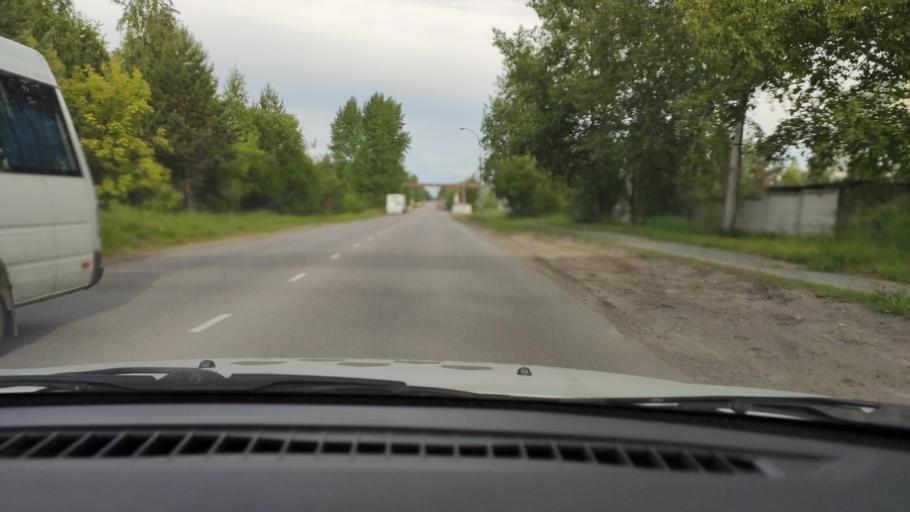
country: RU
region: Perm
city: Overyata
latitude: 58.0167
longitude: 55.8868
